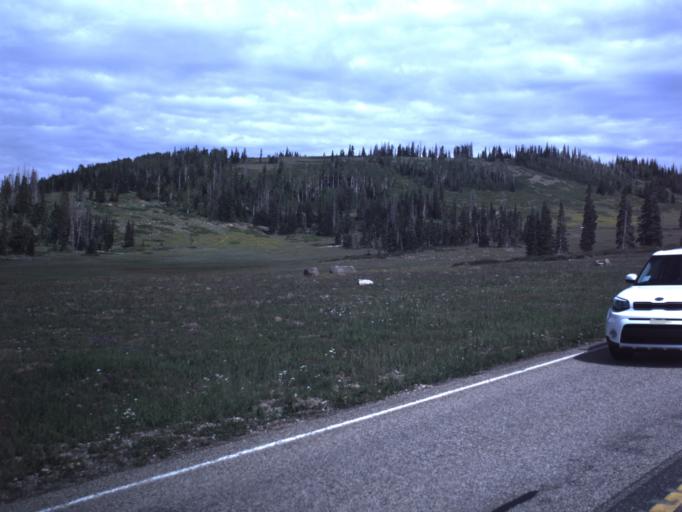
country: US
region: Utah
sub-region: Iron County
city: Cedar City
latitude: 37.5943
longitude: -112.8495
